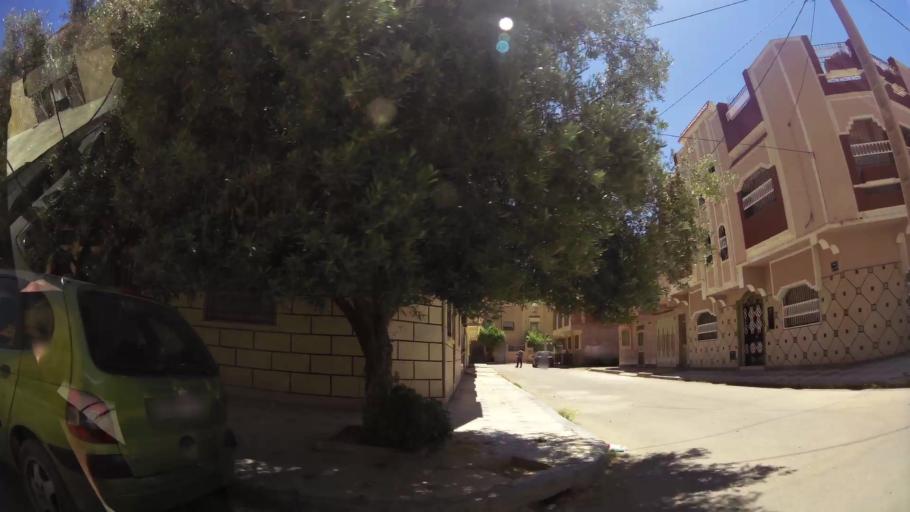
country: MA
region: Oriental
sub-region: Oujda-Angad
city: Oujda
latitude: 34.6730
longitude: -1.8913
